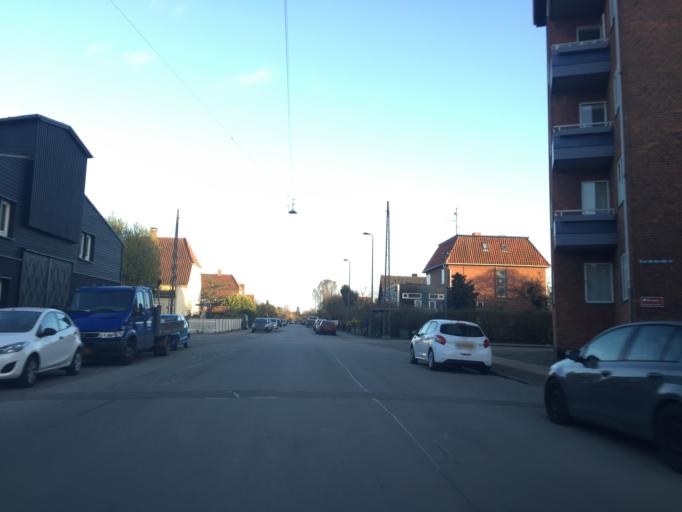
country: DK
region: Capital Region
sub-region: Kobenhavn
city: Christianshavn
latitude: 55.6608
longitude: 12.6253
